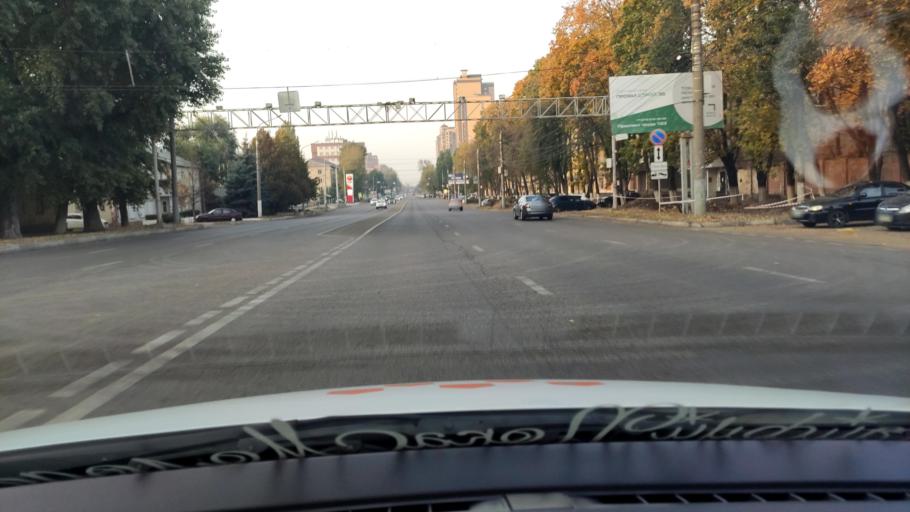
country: RU
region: Voronezj
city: Voronezh
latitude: 51.6777
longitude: 39.1725
